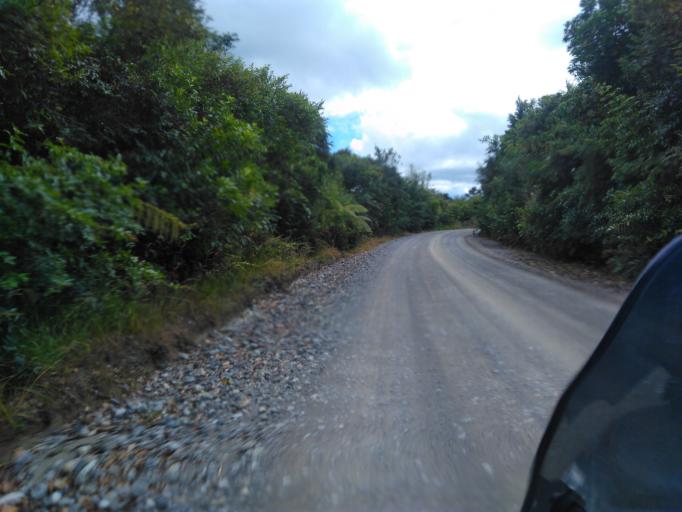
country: NZ
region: Gisborne
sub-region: Gisborne District
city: Gisborne
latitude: -38.2425
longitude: 178.0687
